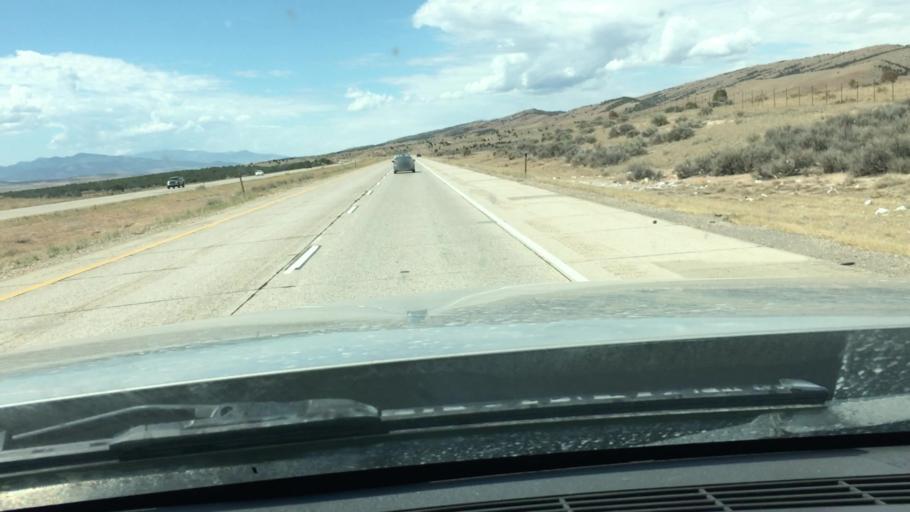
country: US
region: Utah
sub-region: Juab County
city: Nephi
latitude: 39.5629
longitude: -111.9425
